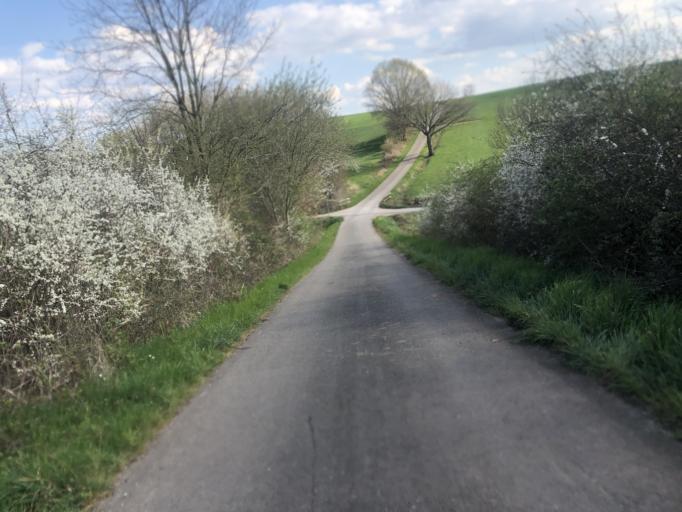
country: DE
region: North Rhine-Westphalia
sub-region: Regierungsbezirk Koln
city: Kall
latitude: 50.5993
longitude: 6.5532
